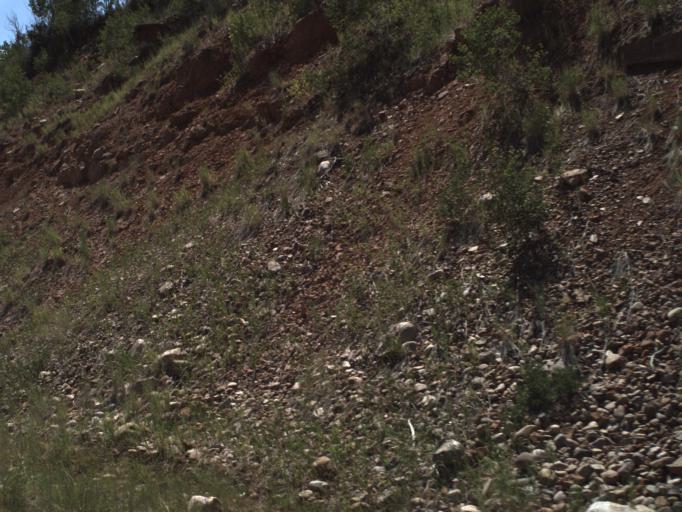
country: US
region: Utah
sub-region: Weber County
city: Wolf Creek
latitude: 41.4226
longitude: -111.5630
